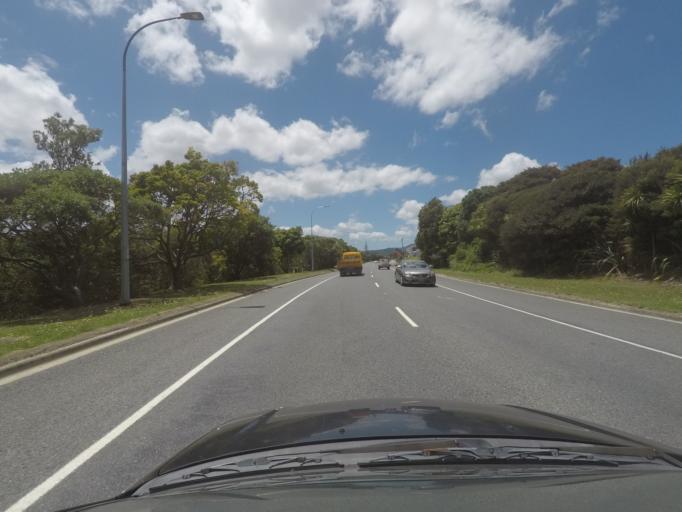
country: NZ
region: Northland
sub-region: Whangarei
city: Whangarei
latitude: -35.7463
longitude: 174.3219
